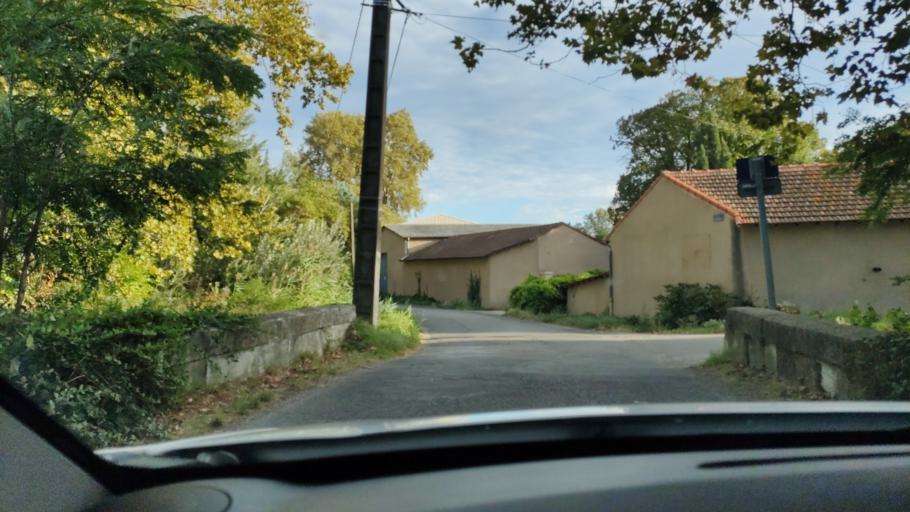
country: FR
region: Provence-Alpes-Cote d'Azur
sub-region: Departement du Vaucluse
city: Avignon
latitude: 43.9229
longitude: 4.8290
